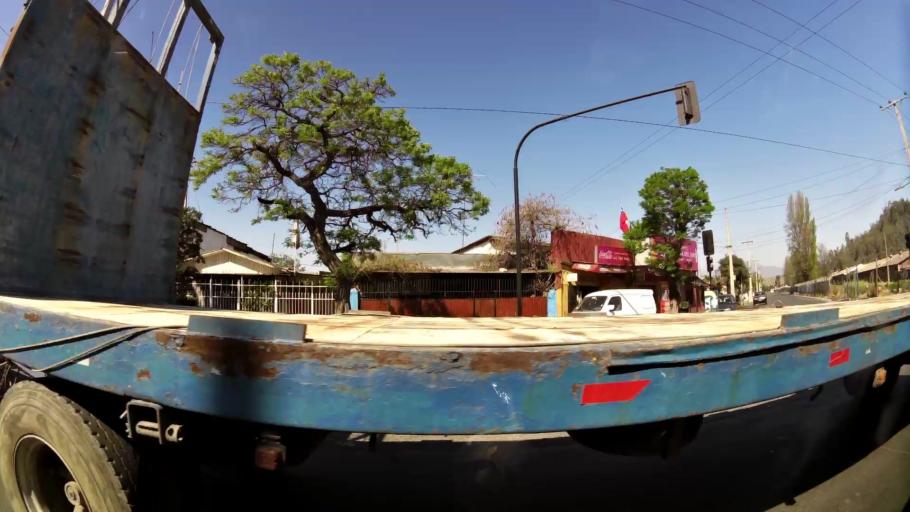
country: CL
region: Santiago Metropolitan
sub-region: Provincia de Maipo
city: San Bernardo
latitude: -33.6045
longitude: -70.7153
